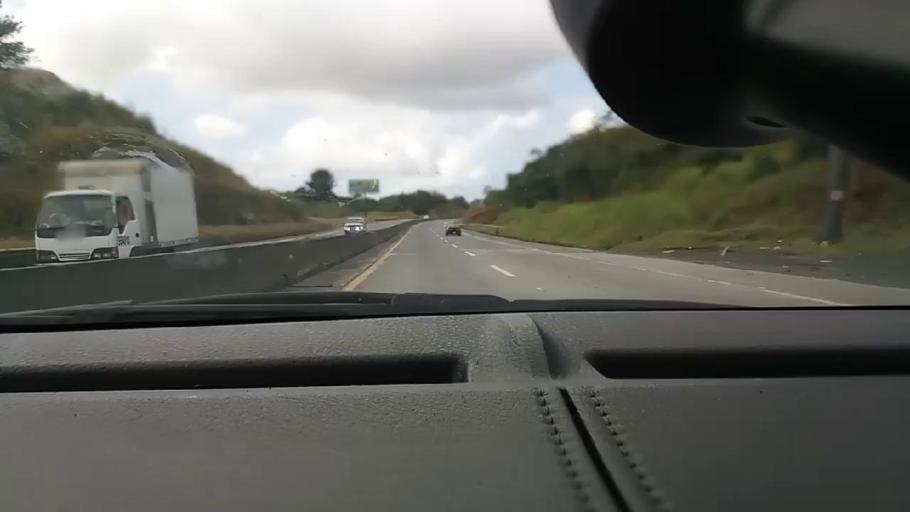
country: PA
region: Colon
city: Gatun
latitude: 9.2820
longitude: -79.7517
